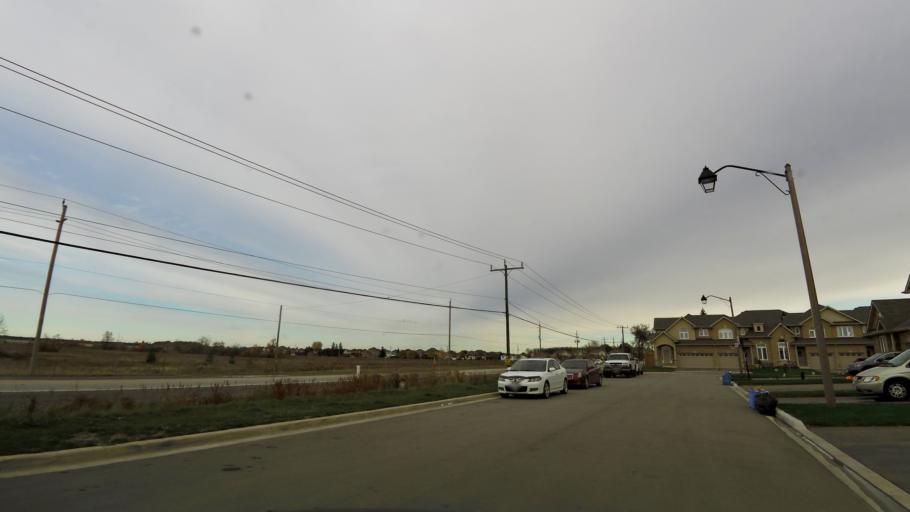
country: CA
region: Ontario
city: Hamilton
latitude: 43.1783
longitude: -79.7999
